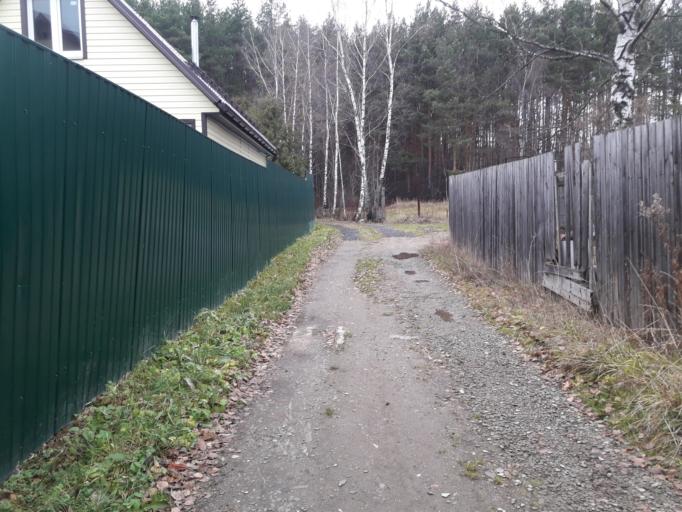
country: RU
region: Moskovskaya
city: Sofrino
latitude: 56.1690
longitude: 37.9283
